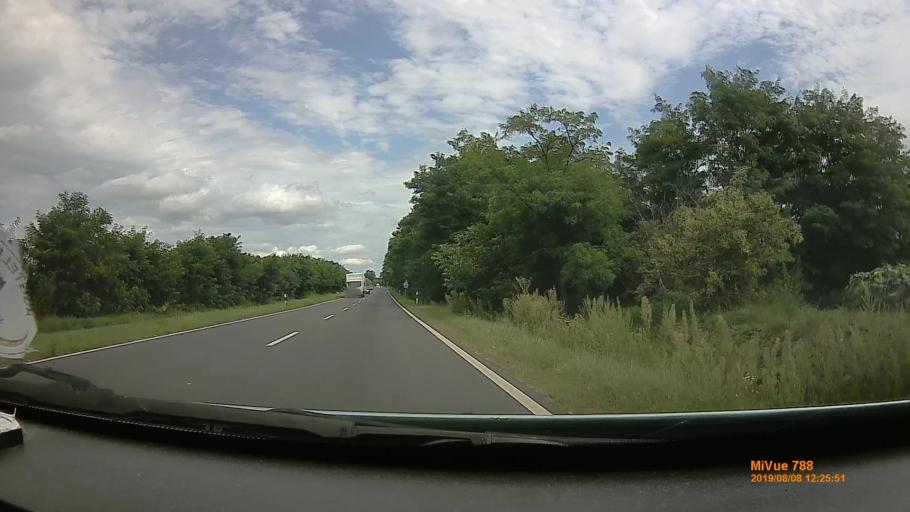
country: HU
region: Szabolcs-Szatmar-Bereg
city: Nyirbogat
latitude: 47.8134
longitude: 22.0783
